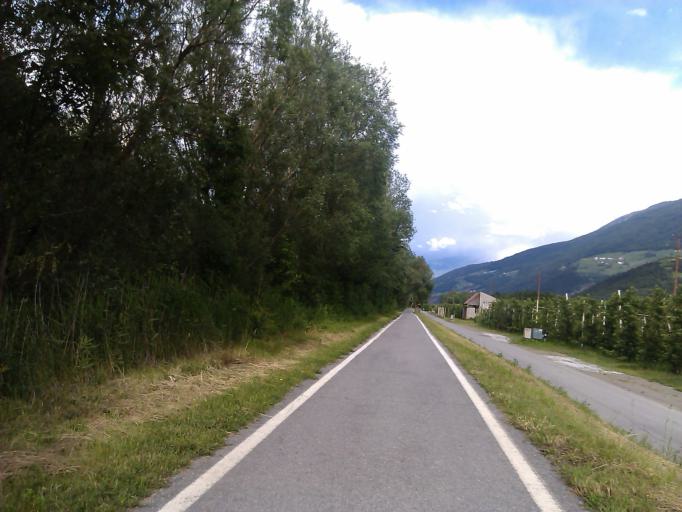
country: IT
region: Trentino-Alto Adige
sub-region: Bolzano
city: Lasa
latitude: 46.6215
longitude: 10.6528
